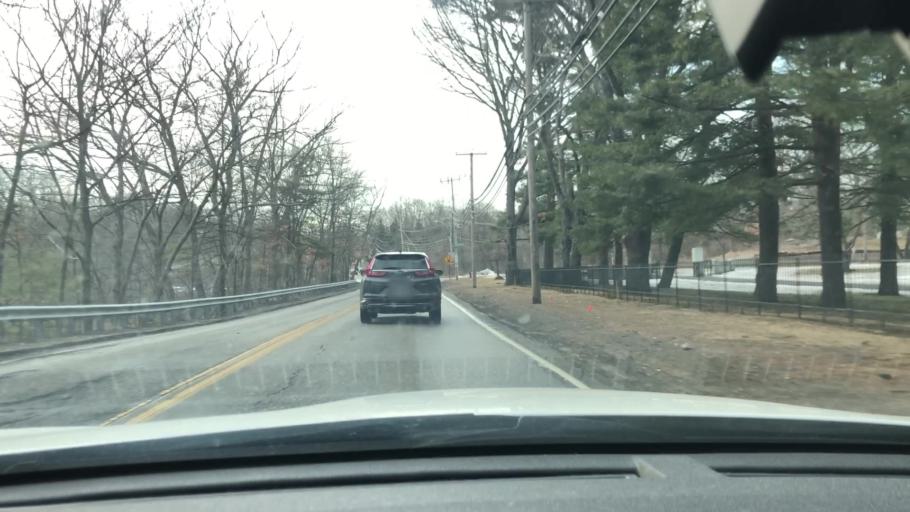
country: US
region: Massachusetts
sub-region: Middlesex County
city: Chelmsford
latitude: 42.5984
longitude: -71.3371
